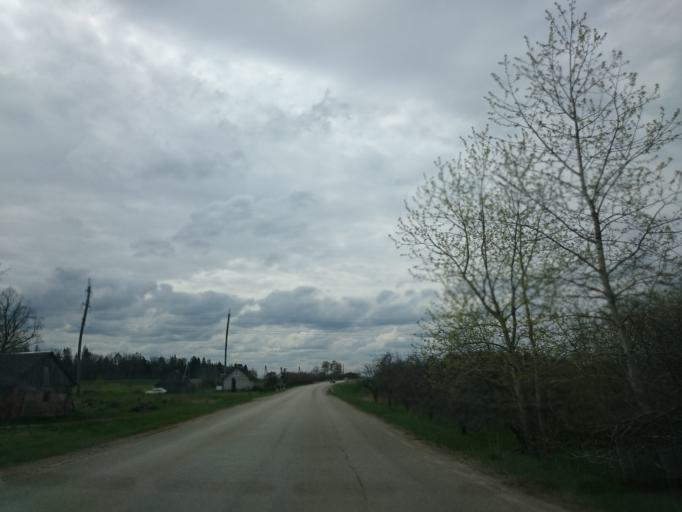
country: LV
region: Tukuma Rajons
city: Tukums
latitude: 56.9288
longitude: 23.0785
